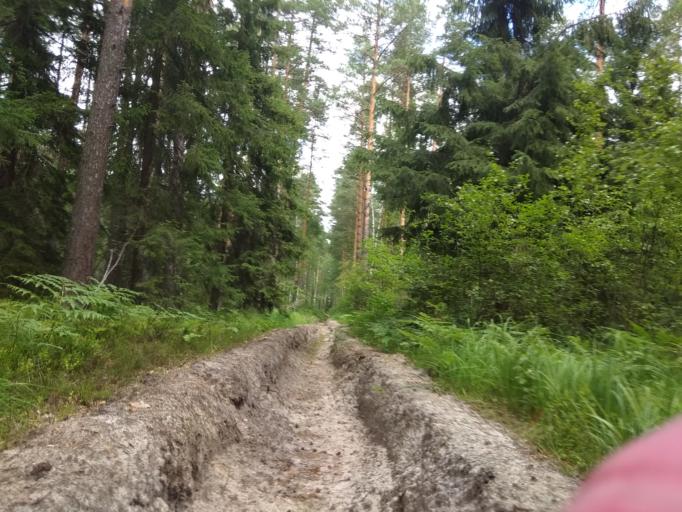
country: RU
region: Moskovskaya
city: Misheronskiy
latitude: 55.6829
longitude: 39.7084
